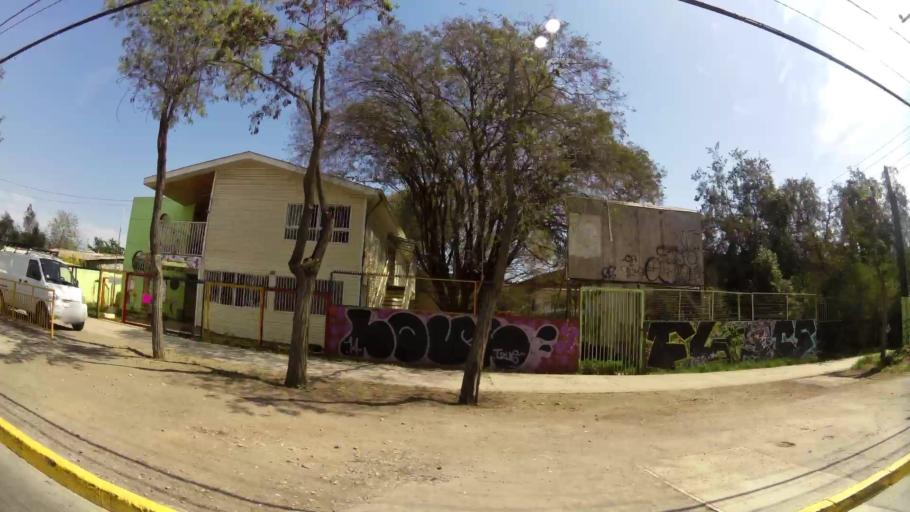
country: CL
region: Santiago Metropolitan
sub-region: Provincia de Santiago
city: La Pintana
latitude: -33.5501
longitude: -70.6678
